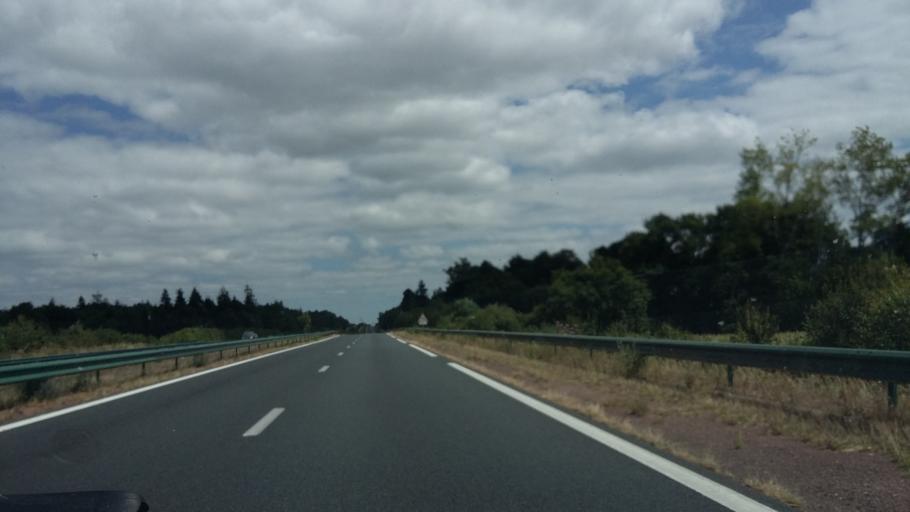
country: FR
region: Pays de la Loire
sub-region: Departement de la Vendee
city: Bournezeau
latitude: 46.6512
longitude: -1.2245
